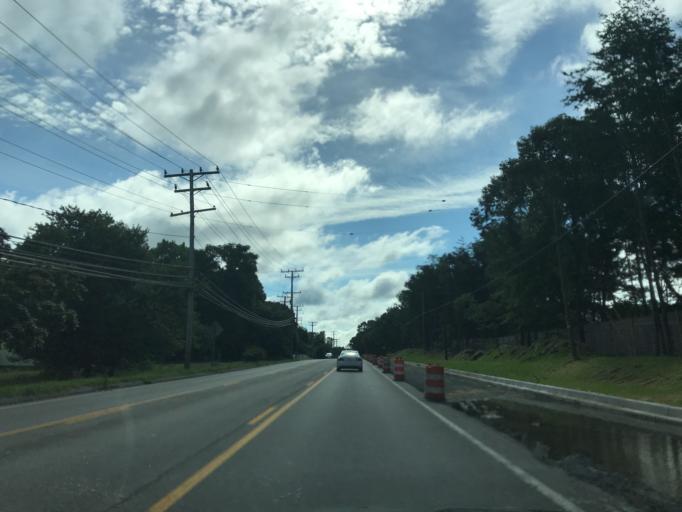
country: US
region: Maryland
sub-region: Anne Arundel County
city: Green Haven
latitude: 39.1301
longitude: -76.5569
